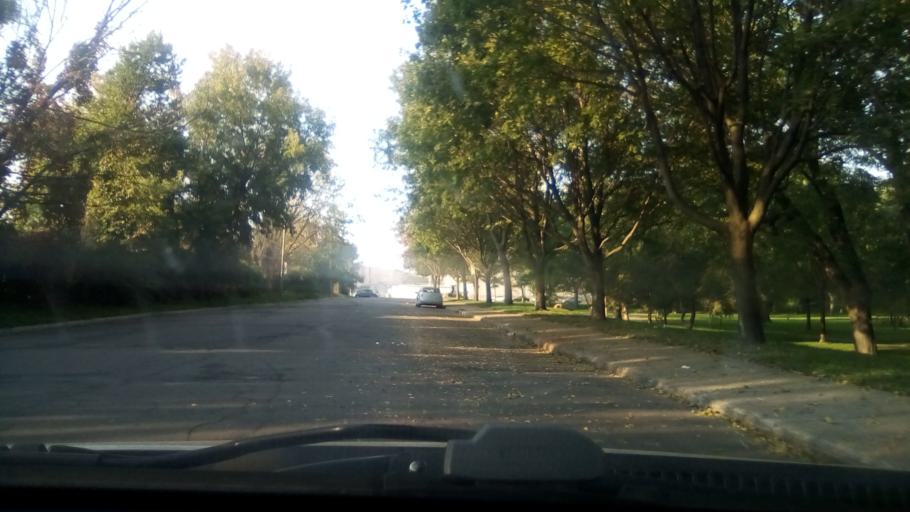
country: CA
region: Quebec
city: Westmount
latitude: 45.4751
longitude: -73.5569
